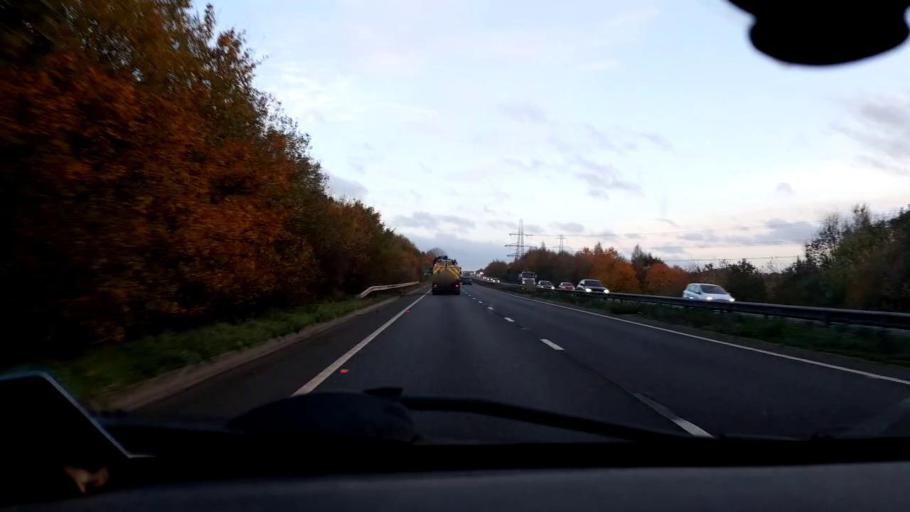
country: GB
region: England
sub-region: Norfolk
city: Bowthorpe
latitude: 52.6126
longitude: 1.2151
